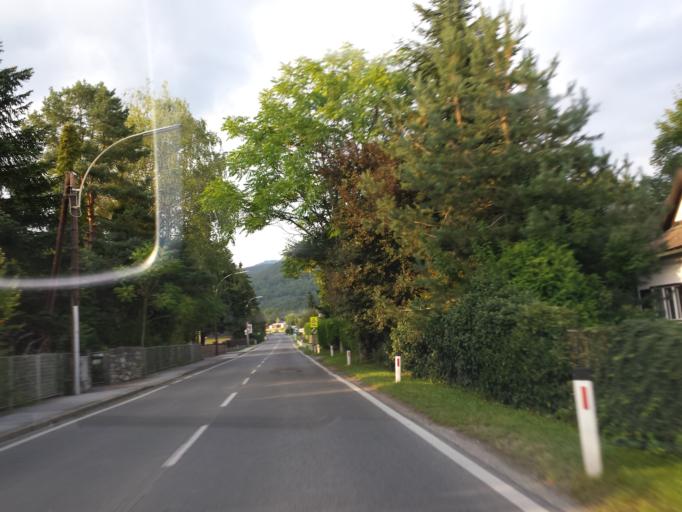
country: AT
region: Styria
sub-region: Politischer Bezirk Graz-Umgebung
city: Stattegg
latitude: 47.1252
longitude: 15.4249
